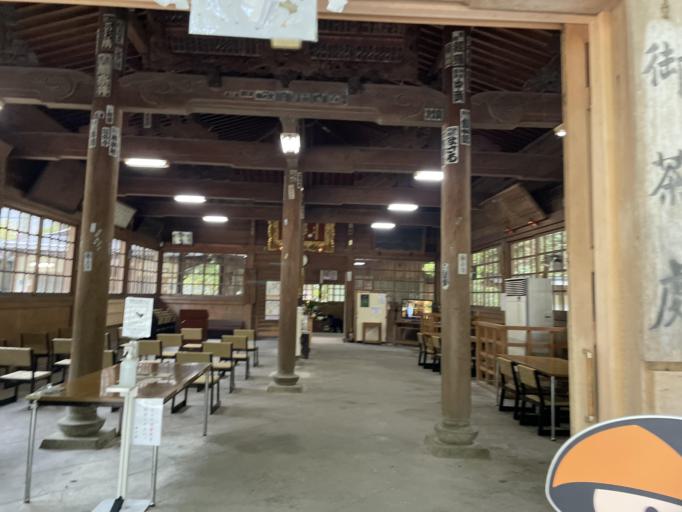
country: JP
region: Wakayama
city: Koya
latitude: 34.2213
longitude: 135.6062
